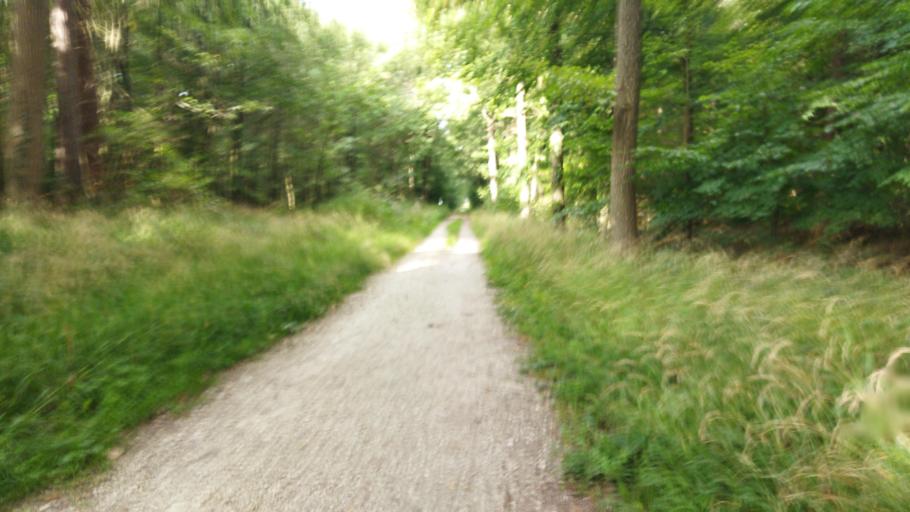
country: DE
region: Lower Saxony
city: Bad Rothenfelde
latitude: 52.0820
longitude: 8.1605
